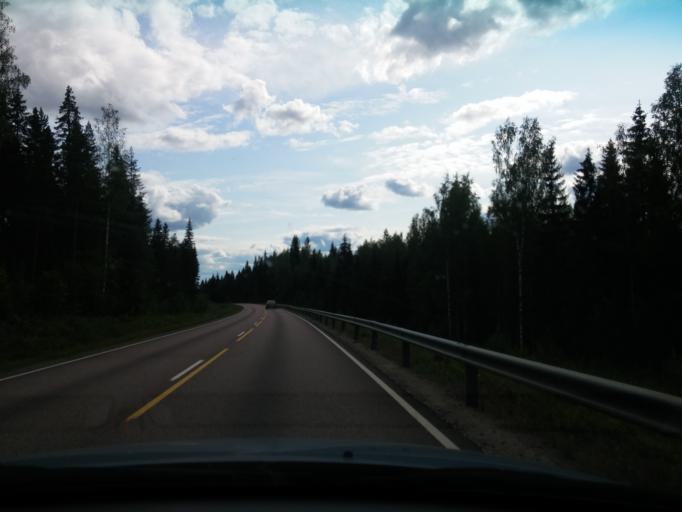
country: FI
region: Central Finland
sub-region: Keuruu
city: Multia
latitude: 62.3750
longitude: 24.7423
